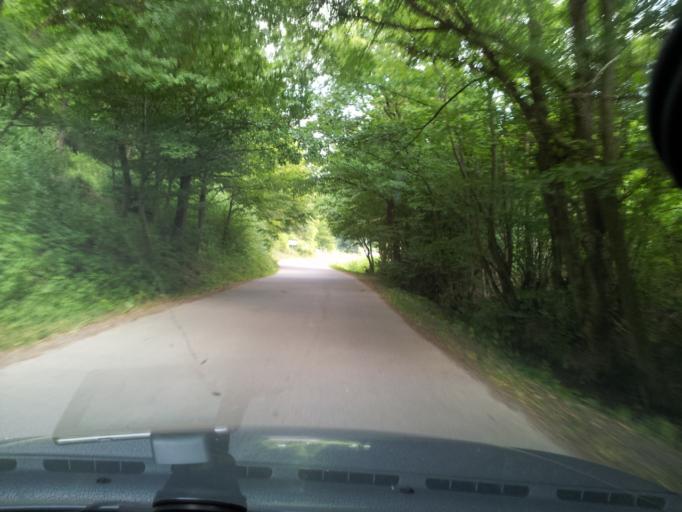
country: SK
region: Trenciansky
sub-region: Okres Trencin
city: Trencin
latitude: 48.8705
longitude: 18.1054
